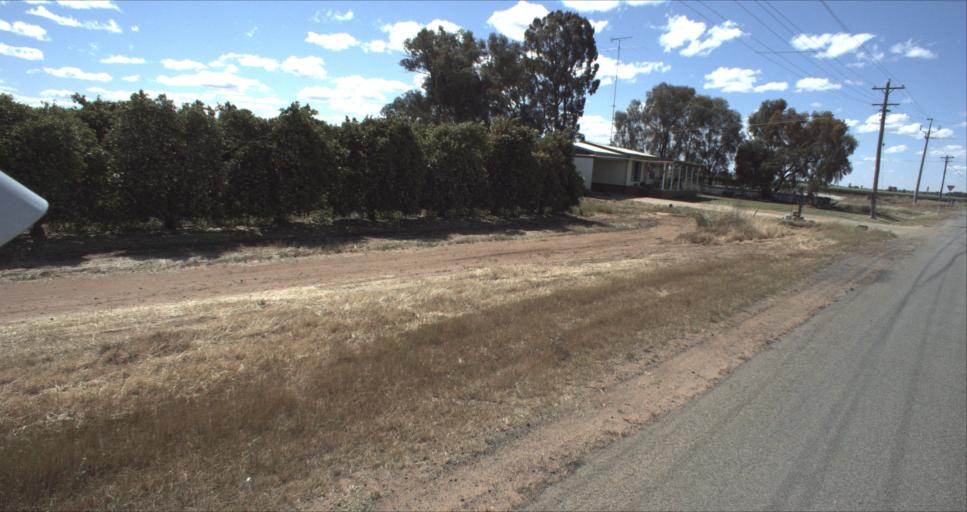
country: AU
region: New South Wales
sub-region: Leeton
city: Leeton
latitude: -34.5094
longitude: 146.2542
